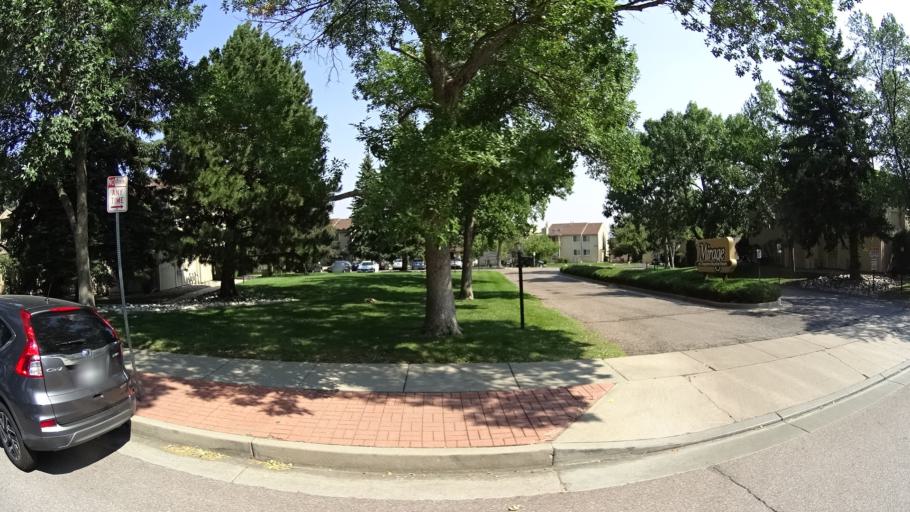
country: US
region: Colorado
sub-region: El Paso County
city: Stratmoor
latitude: 38.7938
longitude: -104.8114
